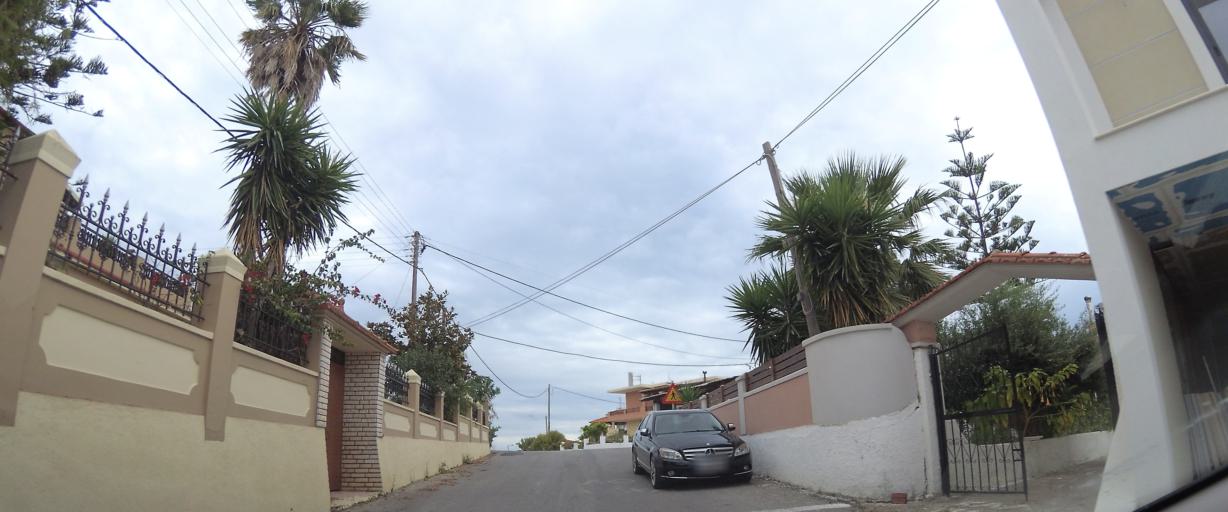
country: GR
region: Ionian Islands
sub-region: Nomos Kerkyras
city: Agios Georgis
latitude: 39.7353
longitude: 19.6676
